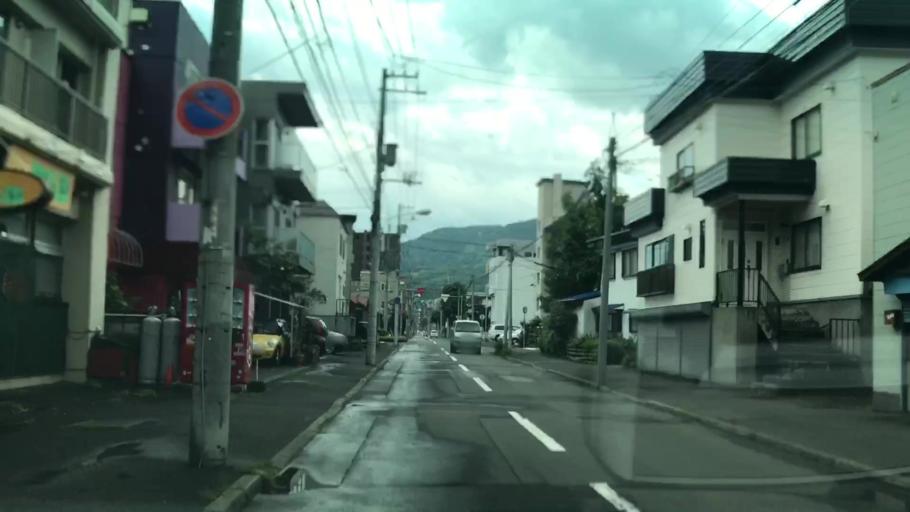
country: JP
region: Hokkaido
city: Sapporo
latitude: 43.0540
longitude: 141.3222
